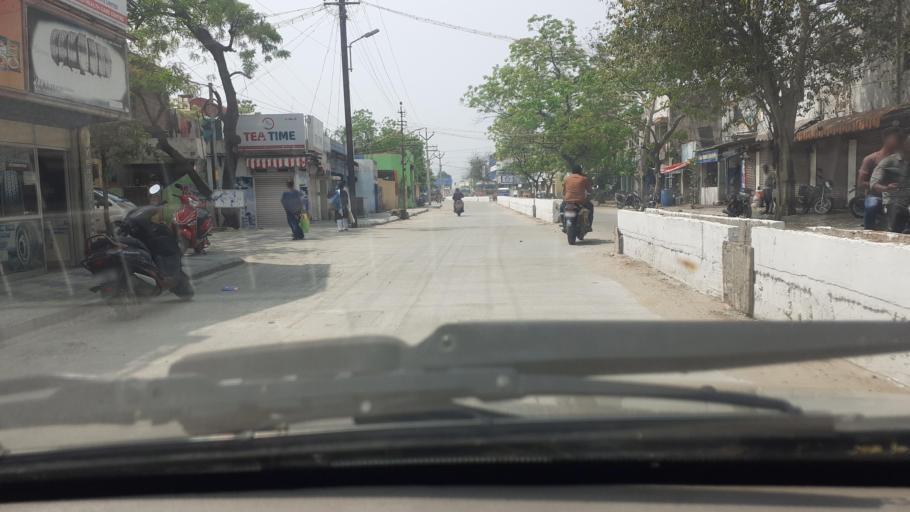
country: IN
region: Tamil Nadu
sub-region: Thoothukkudi
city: Korampallam
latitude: 8.8050
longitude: 78.1387
